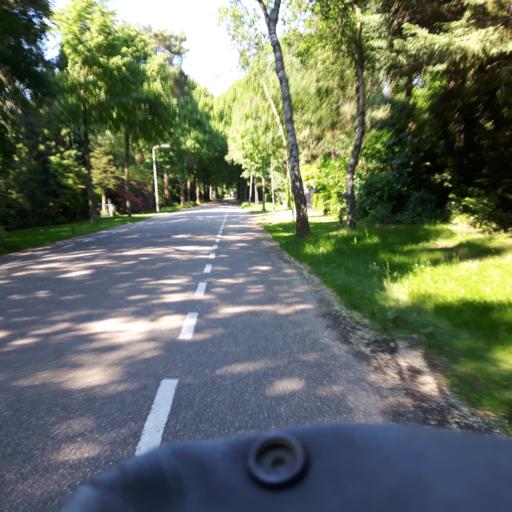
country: NL
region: Utrecht
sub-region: Gemeente Zeist
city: Zeist
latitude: 52.1347
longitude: 5.2403
